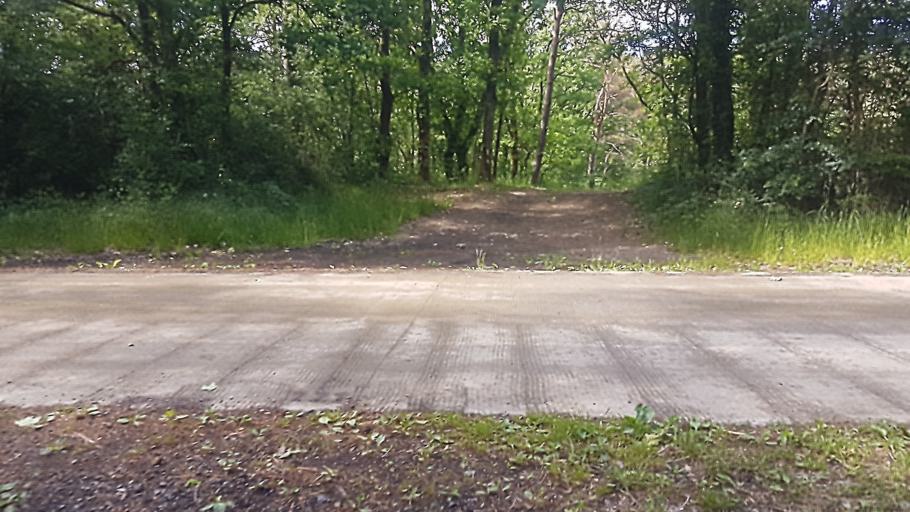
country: BE
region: Wallonia
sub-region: Province de Namur
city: Couvin
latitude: 50.0766
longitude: 4.6041
